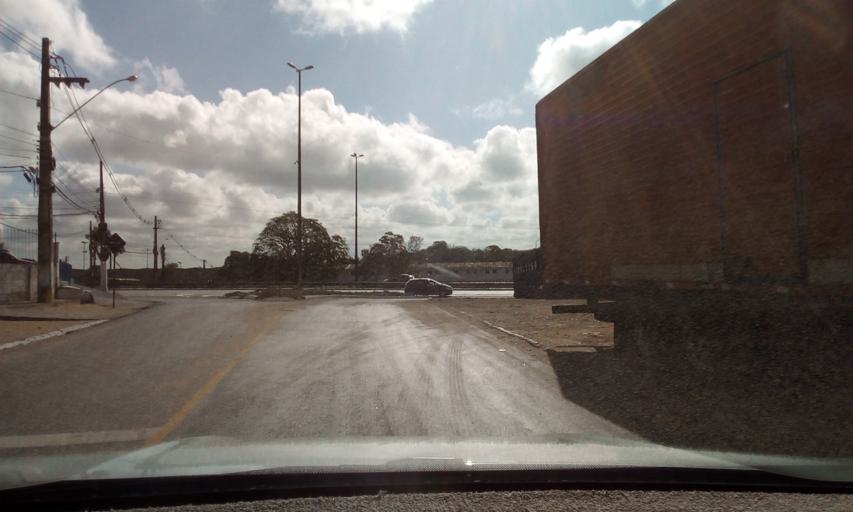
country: BR
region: Paraiba
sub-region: Bayeux
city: Bayeux
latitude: -7.1577
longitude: -34.9060
